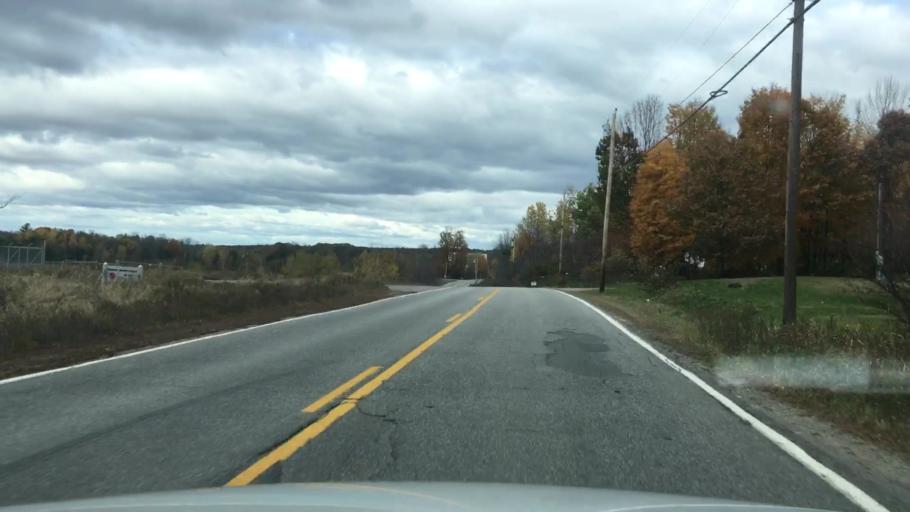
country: US
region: Maine
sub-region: Androscoggin County
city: Sabattus
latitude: 44.1459
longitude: -70.0849
